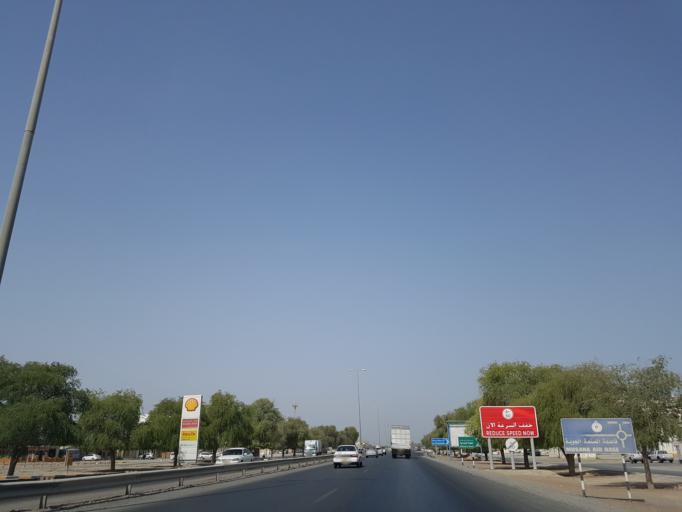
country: OM
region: Al Batinah
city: As Suwayq
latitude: 23.7555
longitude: 57.5823
